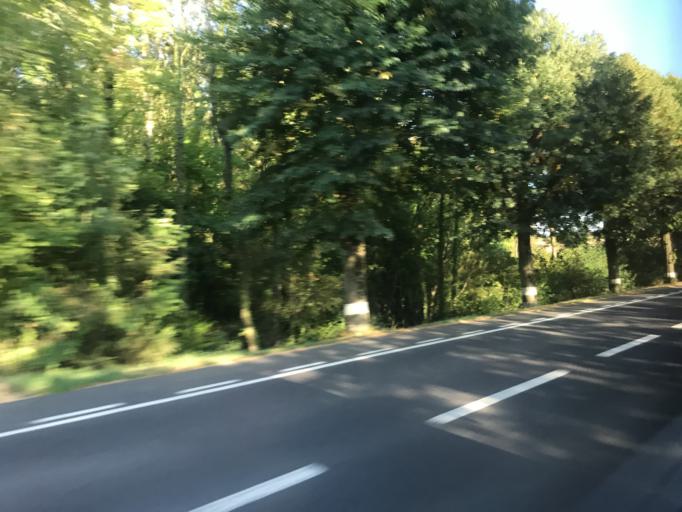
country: LU
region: Luxembourg
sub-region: Canton de Luxembourg
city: Alzingen
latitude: 49.5501
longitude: 6.1729
